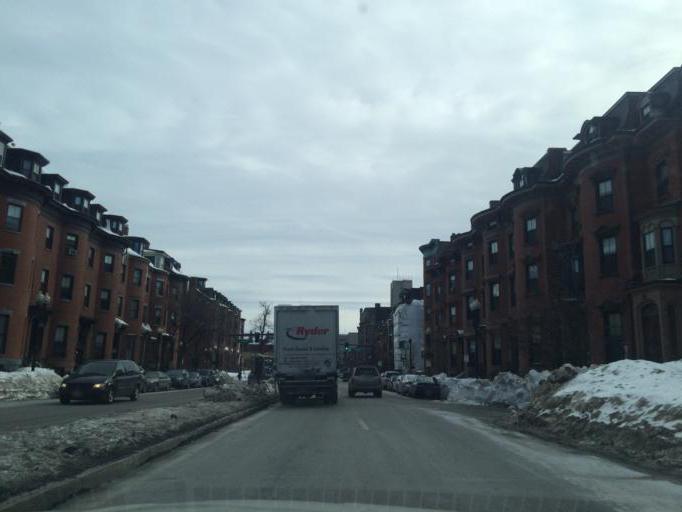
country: US
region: Massachusetts
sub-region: Suffolk County
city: Boston
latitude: 42.3380
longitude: -71.0788
